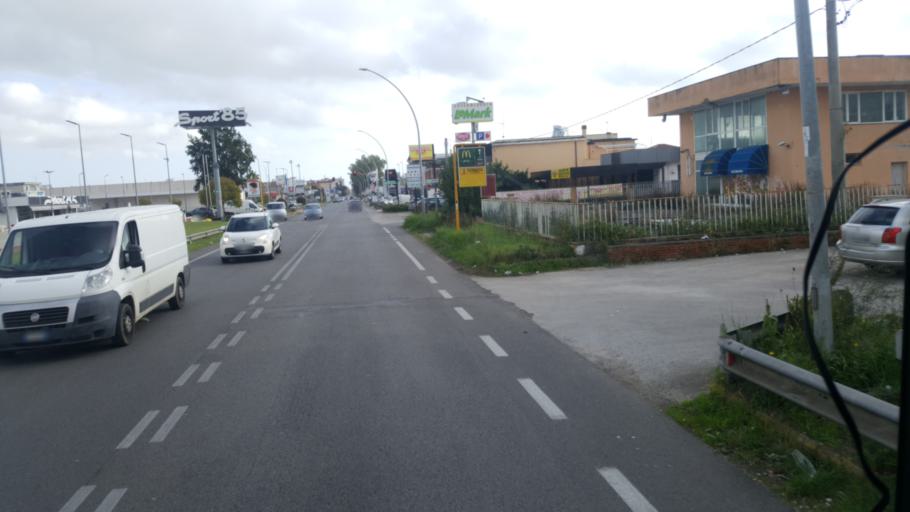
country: IT
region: Latium
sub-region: Provincia di Latina
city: Latina
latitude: 41.4760
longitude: 12.8797
